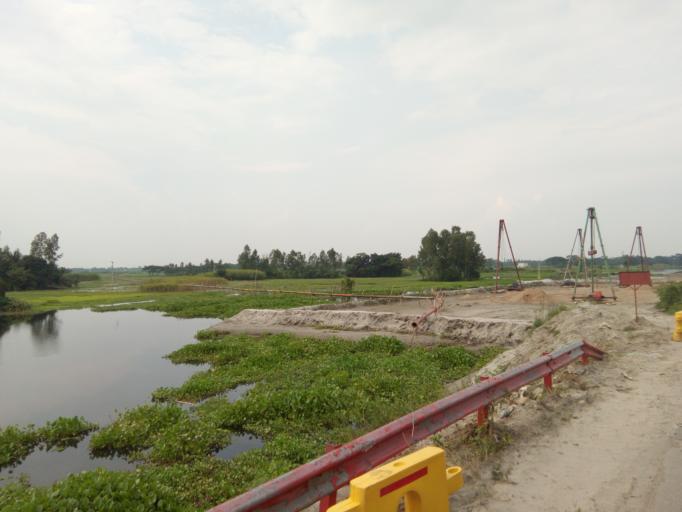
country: BD
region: Dhaka
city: Dohar
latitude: 23.5663
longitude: 90.2997
